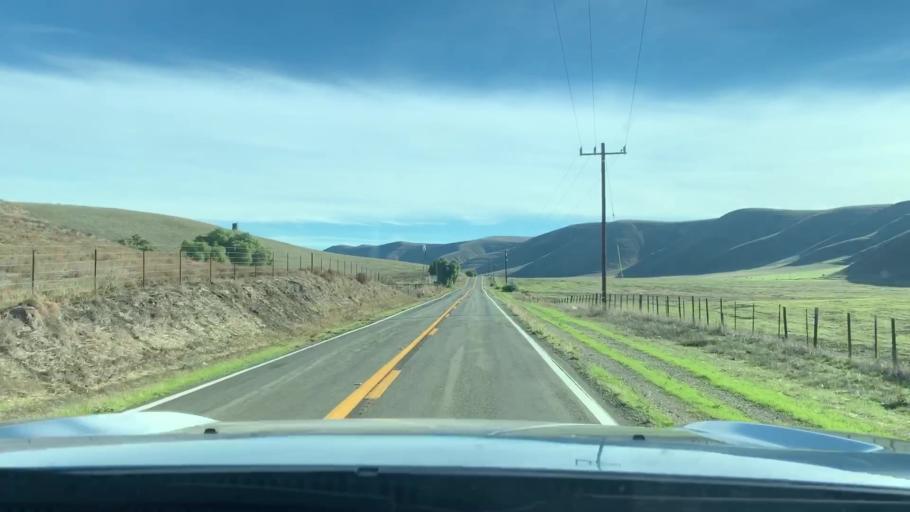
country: US
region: California
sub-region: Monterey County
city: King City
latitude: 36.1501
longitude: -120.9388
